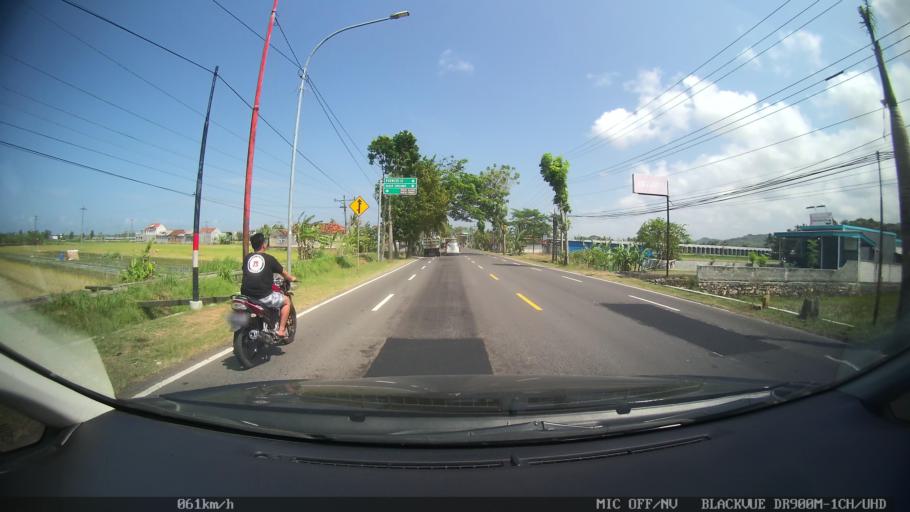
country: ID
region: Daerah Istimewa Yogyakarta
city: Srandakan
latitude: -7.8884
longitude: 110.0947
